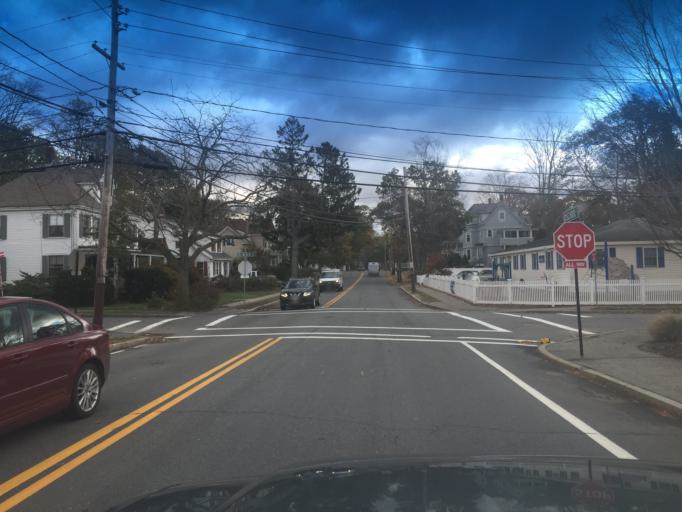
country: US
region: Massachusetts
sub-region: Norfolk County
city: Needham
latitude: 42.2780
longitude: -71.2360
